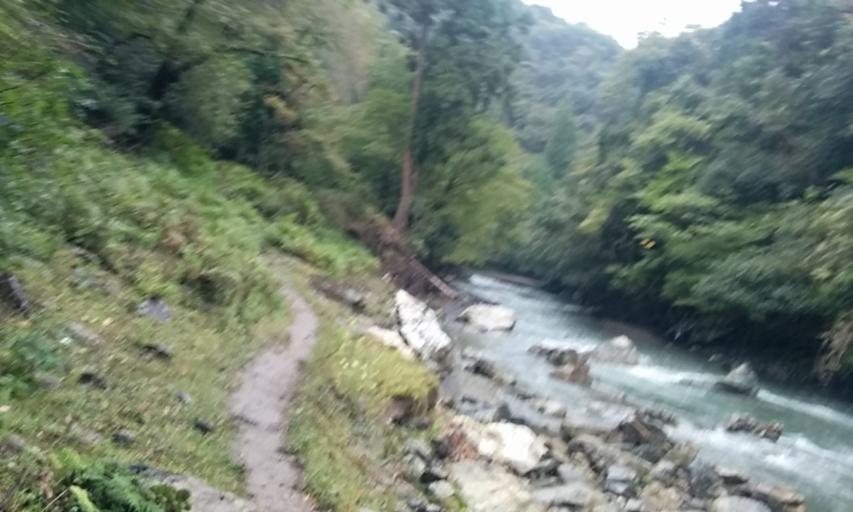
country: JP
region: Kyoto
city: Kameoka
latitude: 35.0485
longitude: 135.6620
